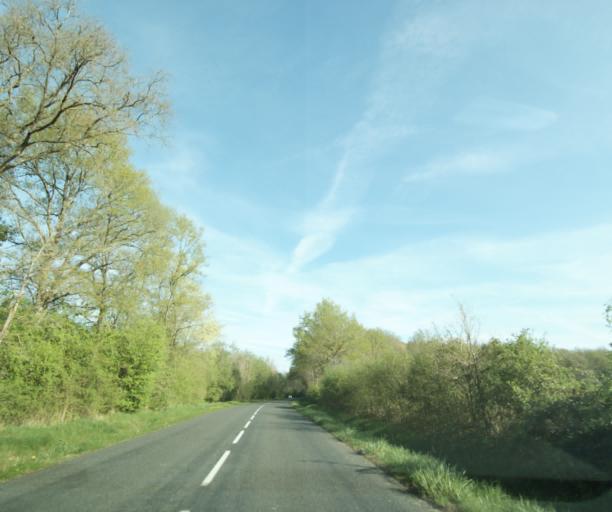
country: FR
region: Ile-de-France
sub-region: Departement de Seine-et-Marne
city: Vernou-la-Celle-sur-Seine
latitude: 48.4680
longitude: 2.8675
